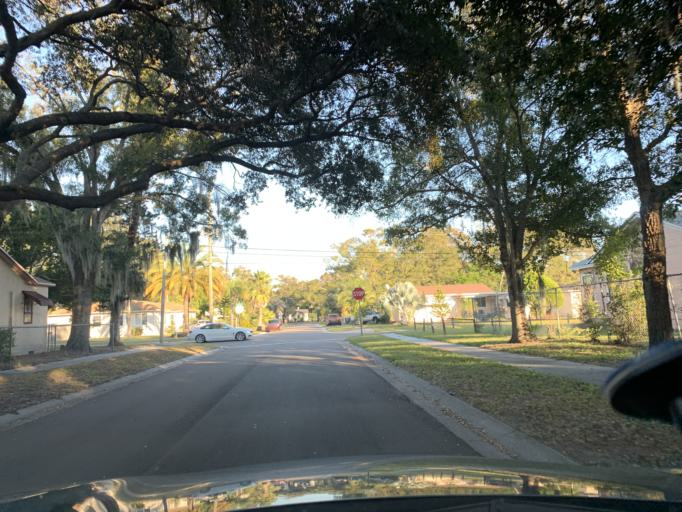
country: US
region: Florida
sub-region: Pinellas County
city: Gulfport
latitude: 27.7475
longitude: -82.6961
